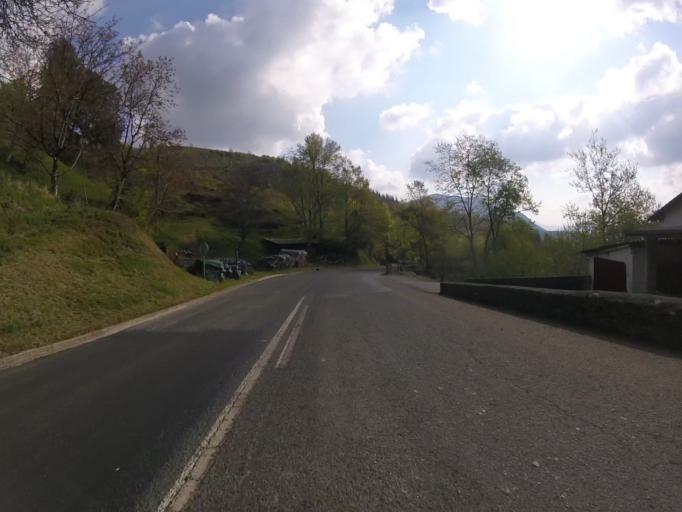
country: ES
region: Basque Country
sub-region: Provincia de Guipuzcoa
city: Azkoitia
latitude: 43.2033
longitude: -2.3583
